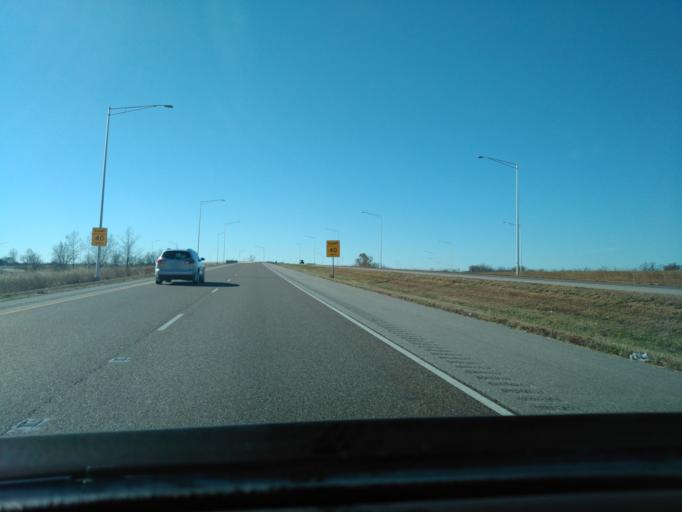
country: US
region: Illinois
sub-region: Saint Clair County
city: Caseyville
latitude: 38.6744
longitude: -90.0312
